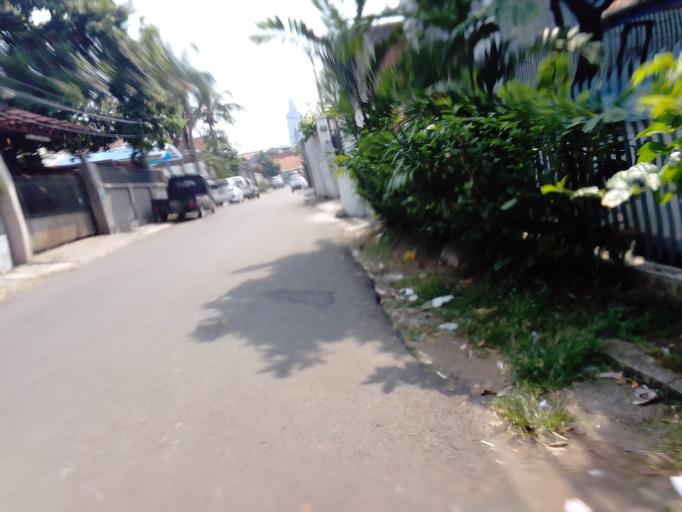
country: ID
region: Jakarta Raya
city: Jakarta
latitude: -6.2184
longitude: 106.7959
